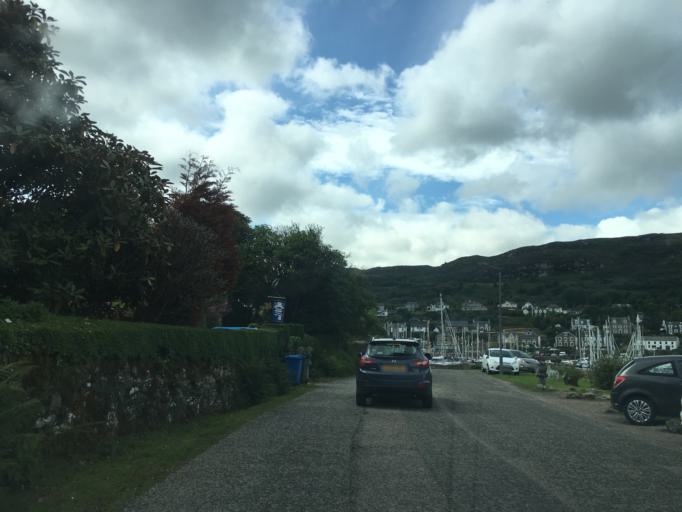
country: GB
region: Scotland
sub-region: Argyll and Bute
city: Tarbert
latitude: 55.8650
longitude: -5.4072
